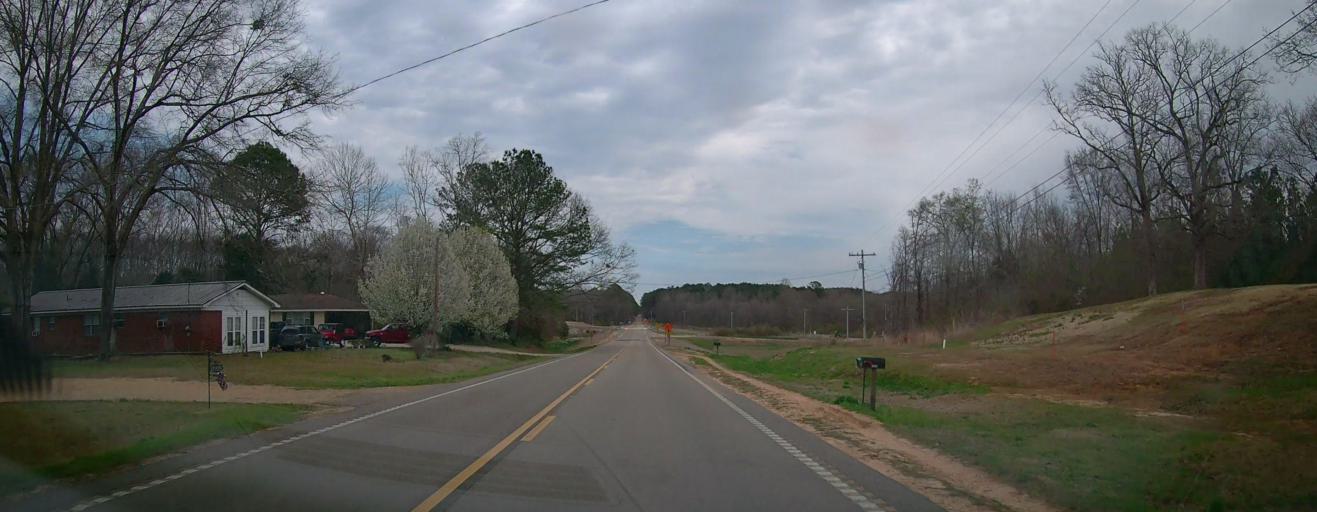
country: US
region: Mississippi
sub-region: Itawamba County
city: Fulton
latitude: 34.2214
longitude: -88.2171
